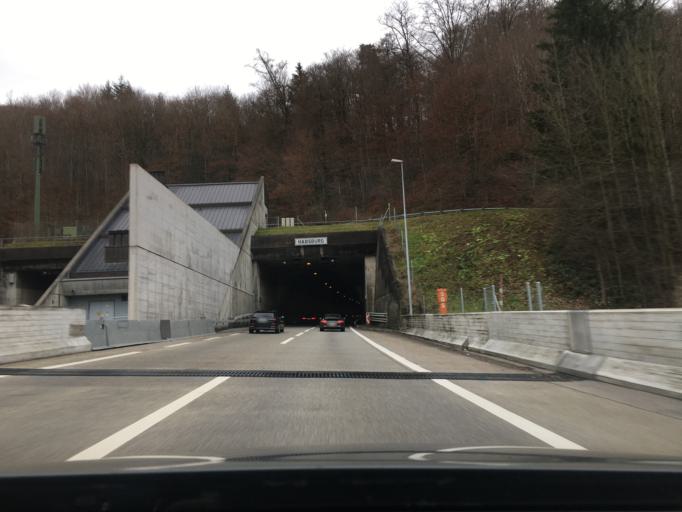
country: CH
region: Aargau
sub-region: Bezirk Brugg
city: Schinznach Bad
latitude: 47.4620
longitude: 8.1725
